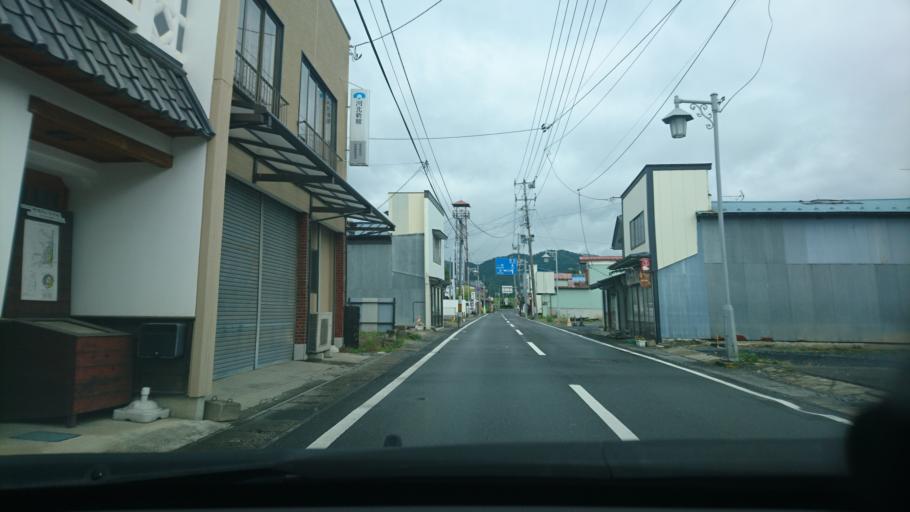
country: JP
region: Miyagi
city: Wakuya
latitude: 38.6514
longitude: 141.2800
